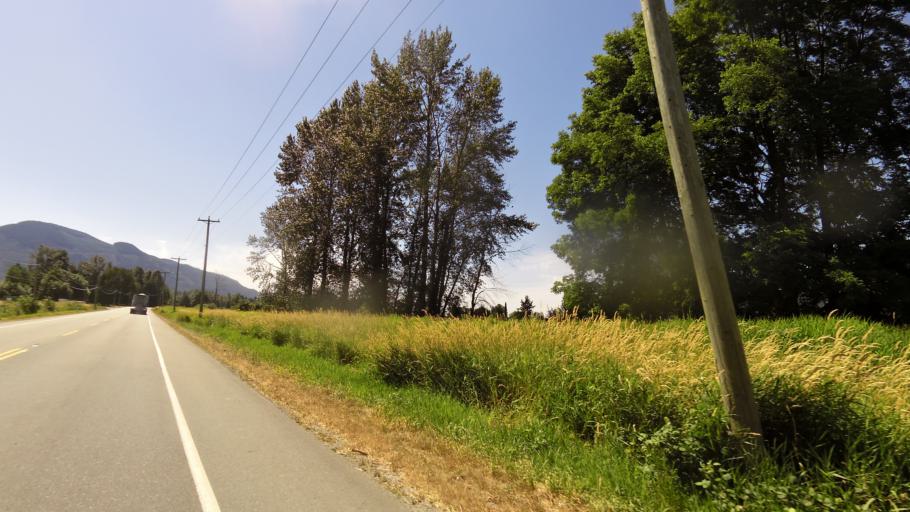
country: CA
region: British Columbia
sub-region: Fraser Valley Regional District
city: Chilliwack
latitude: 49.1760
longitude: -122.0796
